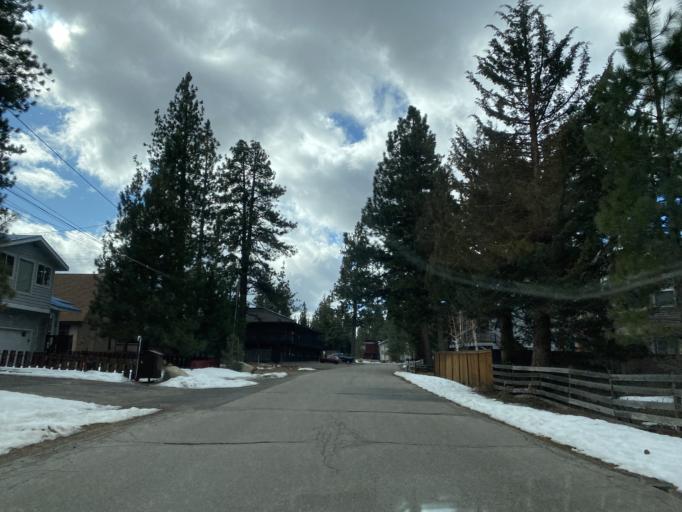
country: US
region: California
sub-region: El Dorado County
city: South Lake Tahoe
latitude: 38.9591
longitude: -119.9484
